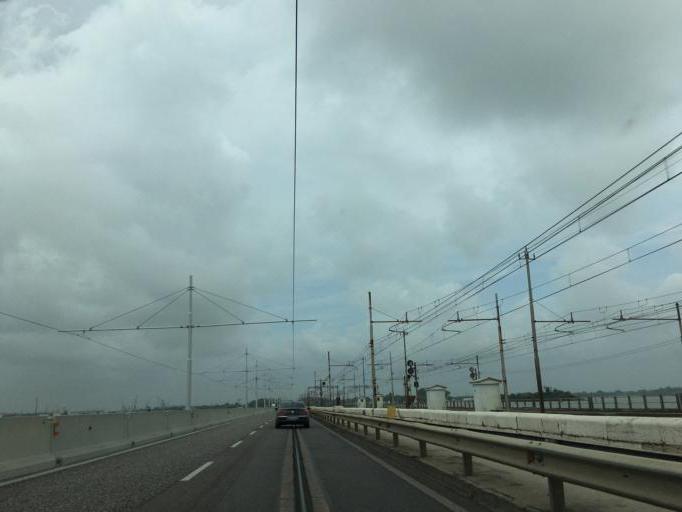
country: IT
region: Veneto
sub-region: Provincia di Venezia
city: Campalto
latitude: 45.4581
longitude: 12.2911
